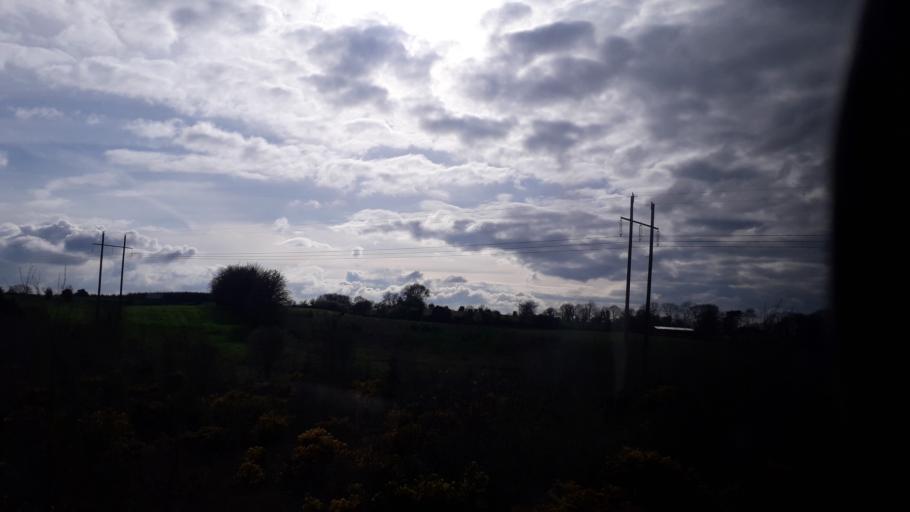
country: IE
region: Leinster
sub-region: An Iarmhi
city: An Muileann gCearr
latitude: 53.5026
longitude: -7.2704
